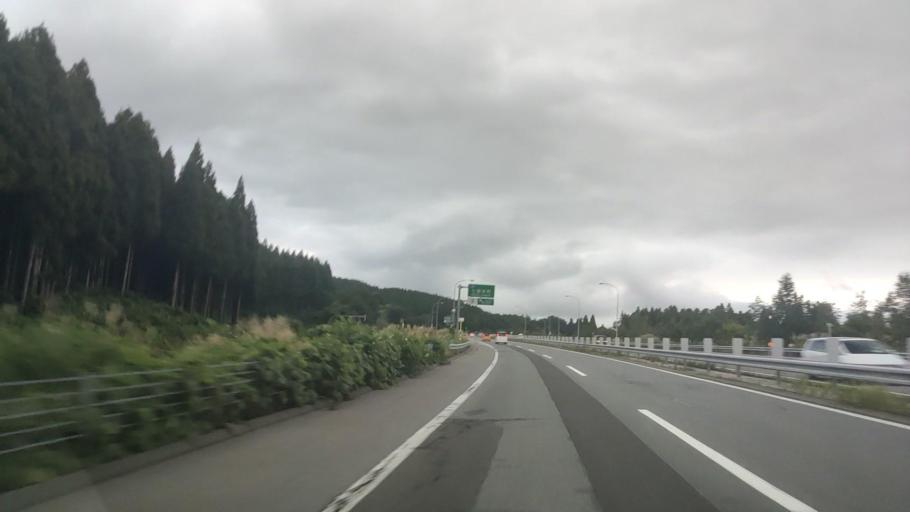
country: JP
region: Hokkaido
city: Nanae
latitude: 41.9017
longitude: 140.7008
